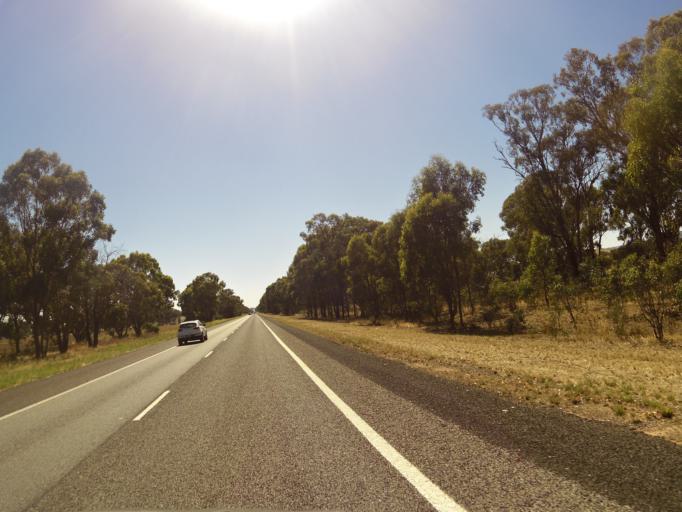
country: AU
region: Victoria
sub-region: Greater Shepparton
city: Shepparton
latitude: -36.8582
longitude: 145.3148
